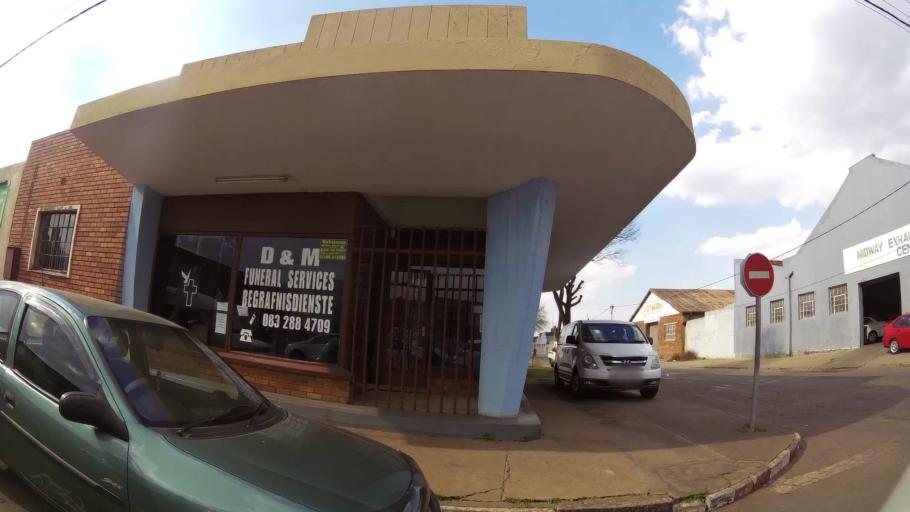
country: ZA
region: Mpumalanga
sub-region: Nkangala District Municipality
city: Delmas
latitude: -26.1494
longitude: 28.6853
